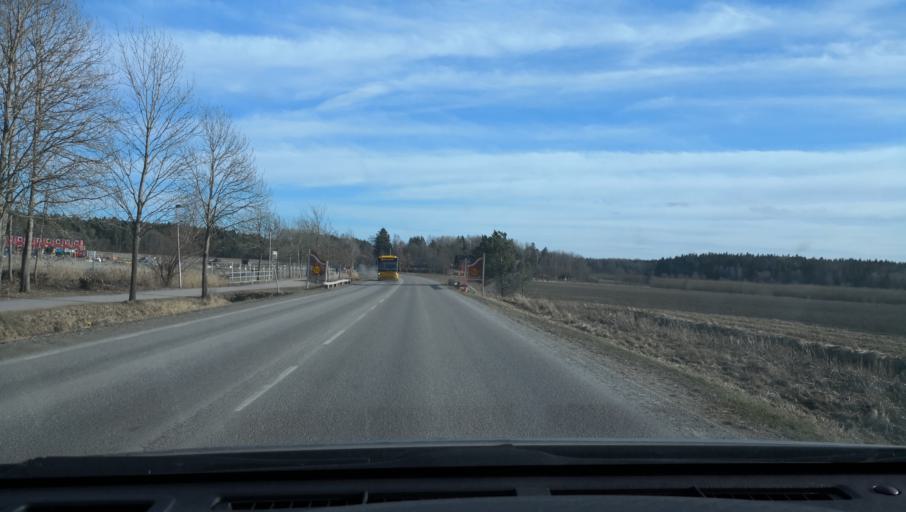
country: SE
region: Uppsala
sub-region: Enkopings Kommun
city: Enkoping
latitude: 59.6304
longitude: 17.0884
